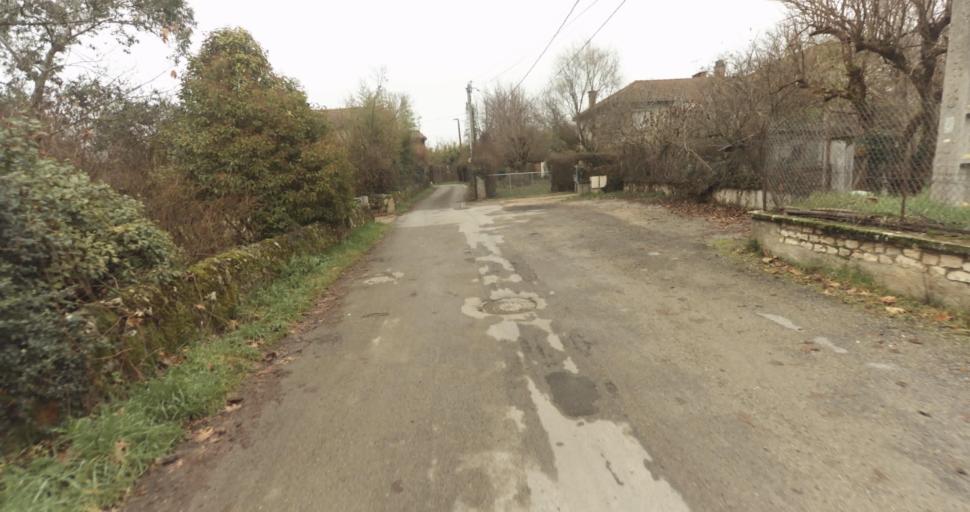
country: FR
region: Midi-Pyrenees
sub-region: Departement du Lot
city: Figeac
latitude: 44.6062
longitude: 2.0212
